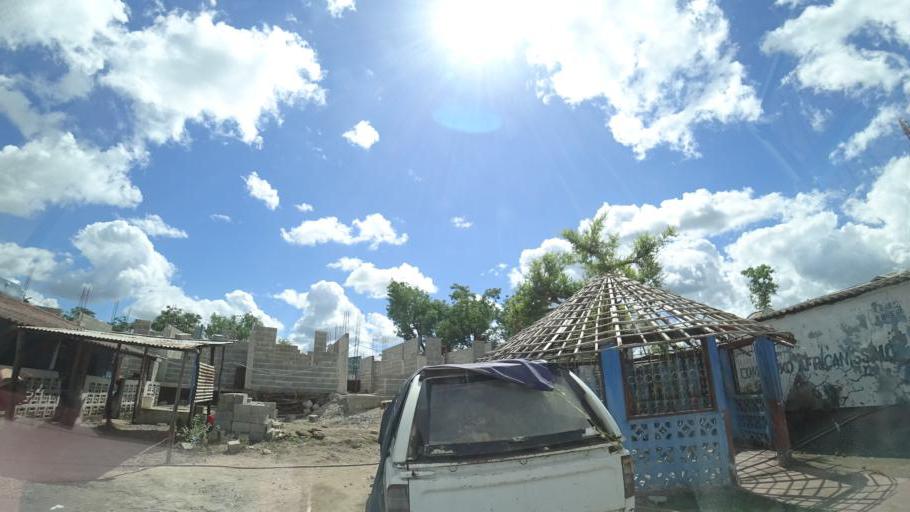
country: MZ
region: Sofala
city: Dondo
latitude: -19.2726
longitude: 34.2038
